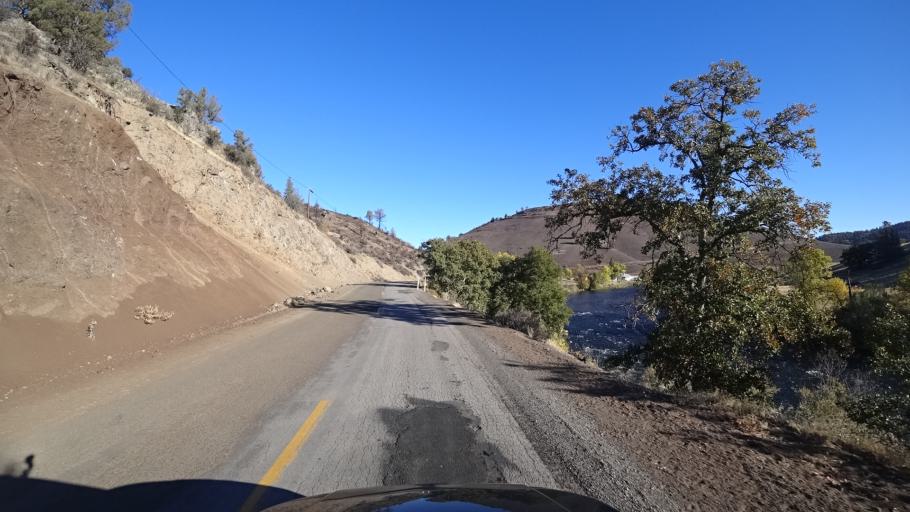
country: US
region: California
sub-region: Siskiyou County
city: Montague
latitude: 41.9145
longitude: -122.4619
